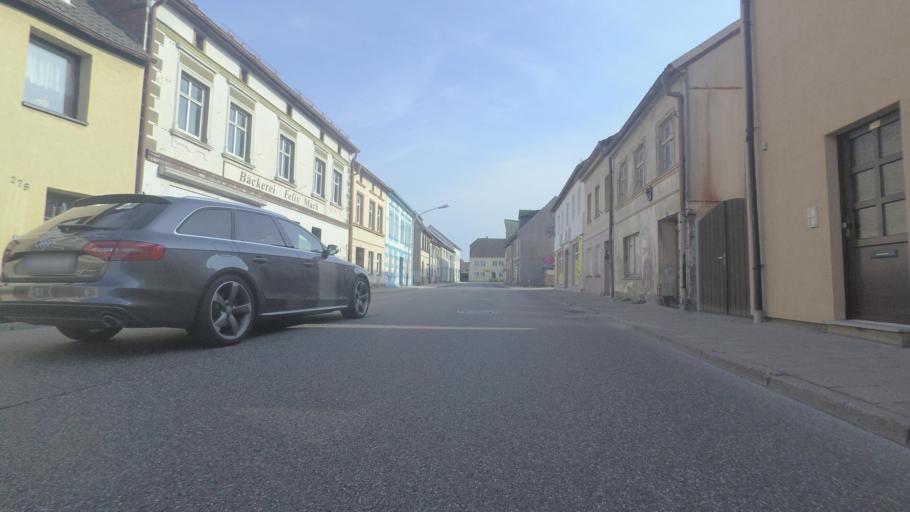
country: DE
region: Mecklenburg-Vorpommern
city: Demmin
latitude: 53.9719
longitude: 13.1295
